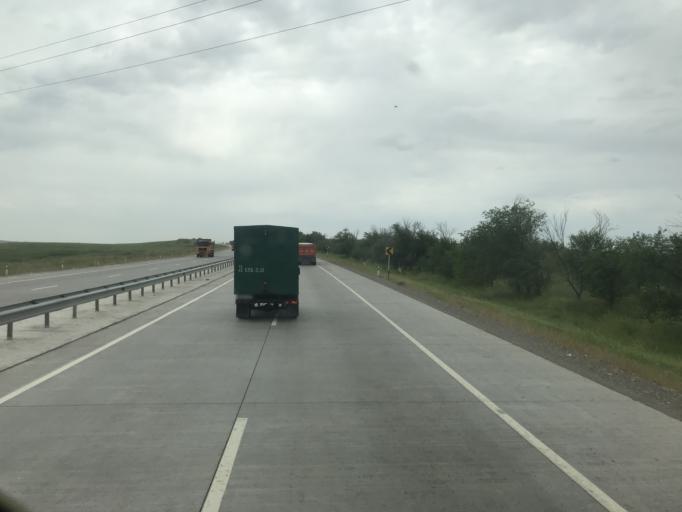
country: KZ
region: Ongtustik Qazaqstan
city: Shymkent
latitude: 42.2045
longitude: 69.5117
